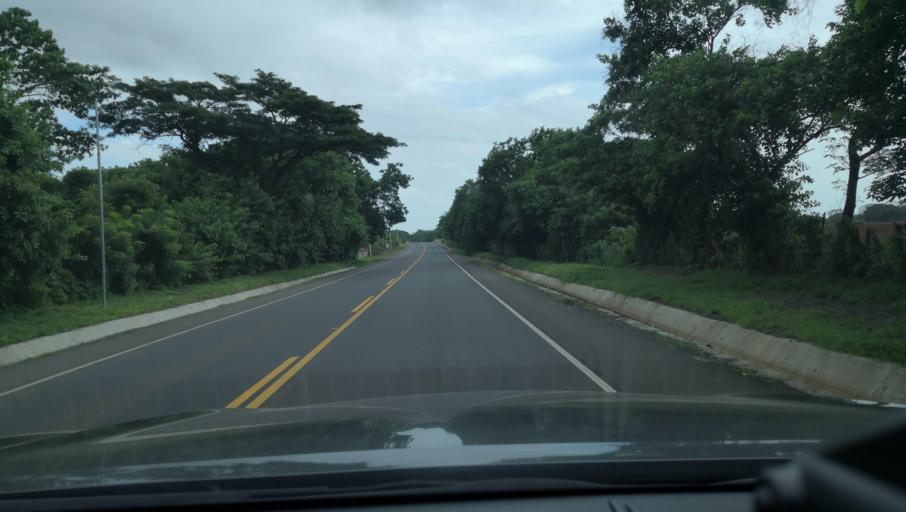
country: NI
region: Masaya
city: Nindiri
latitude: 12.0788
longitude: -86.1383
